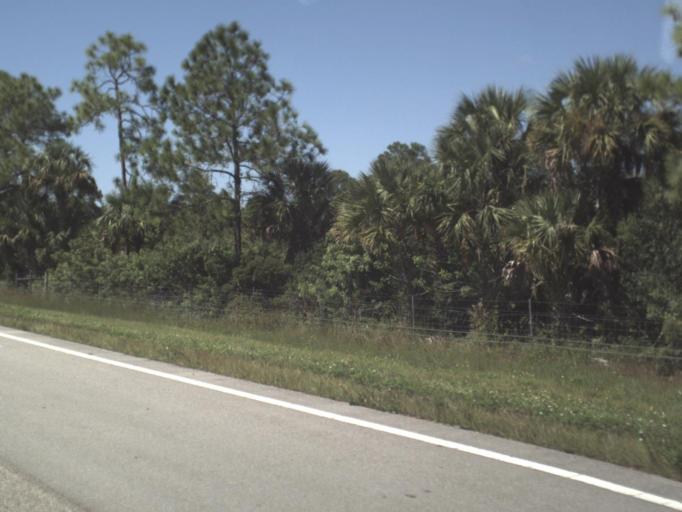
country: US
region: Florida
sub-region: Collier County
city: Orangetree
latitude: 26.1531
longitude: -81.5463
